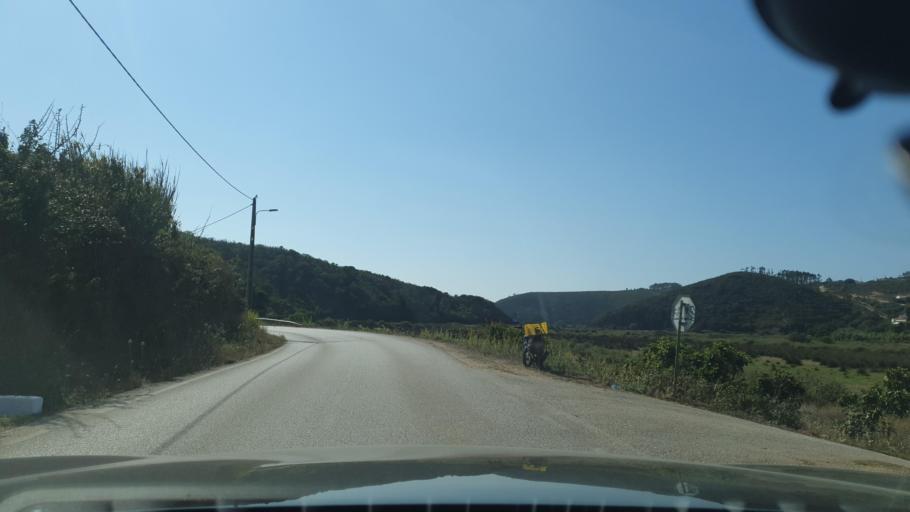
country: PT
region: Beja
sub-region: Odemira
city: Sao Teotonio
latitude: 37.4324
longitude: -8.7815
